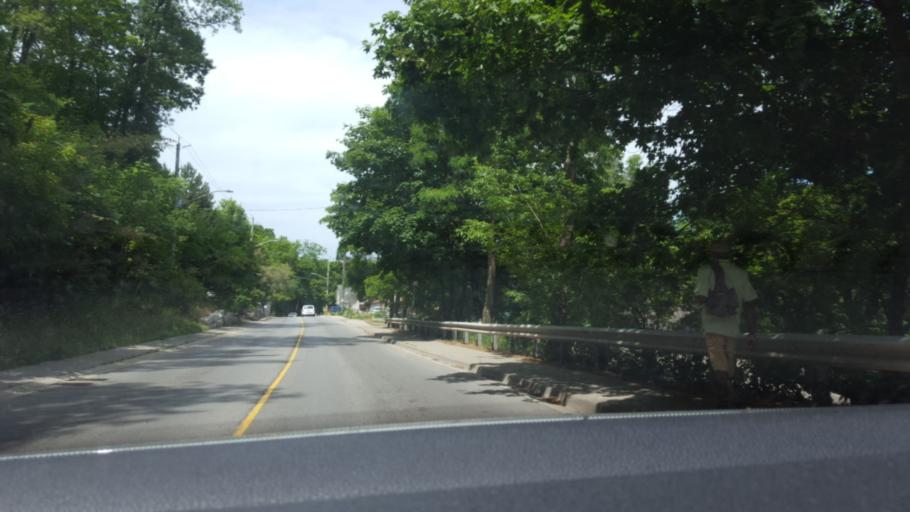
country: CA
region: Ontario
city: Oakville
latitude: 43.1888
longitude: -79.5619
